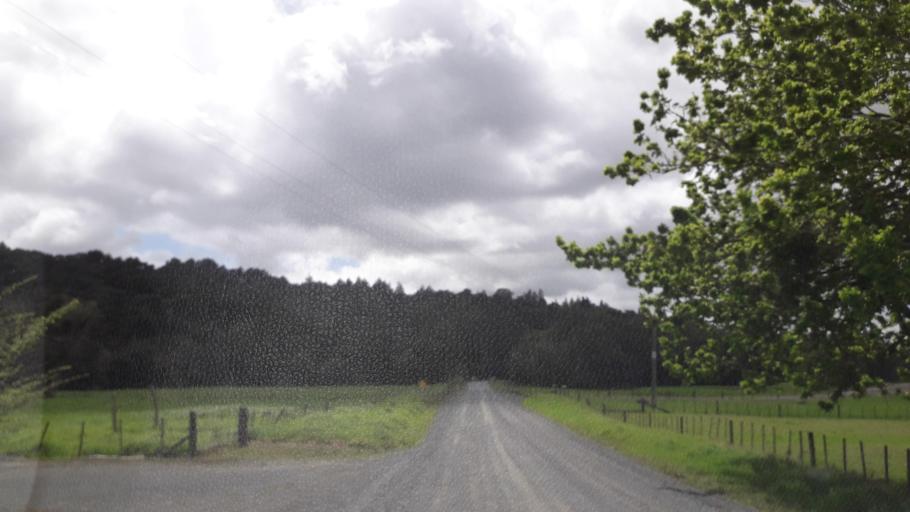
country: NZ
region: Northland
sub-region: Far North District
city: Kaitaia
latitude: -35.1718
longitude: 173.3322
